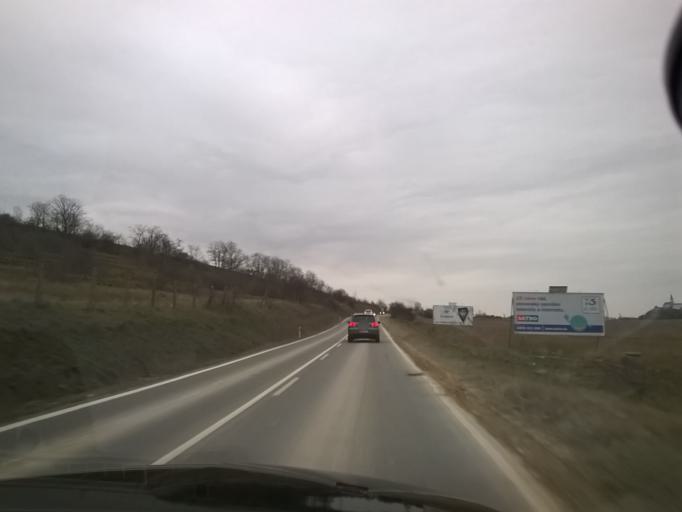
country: SK
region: Nitriansky
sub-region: Okres Nitra
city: Nitra
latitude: 48.3358
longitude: 18.0727
